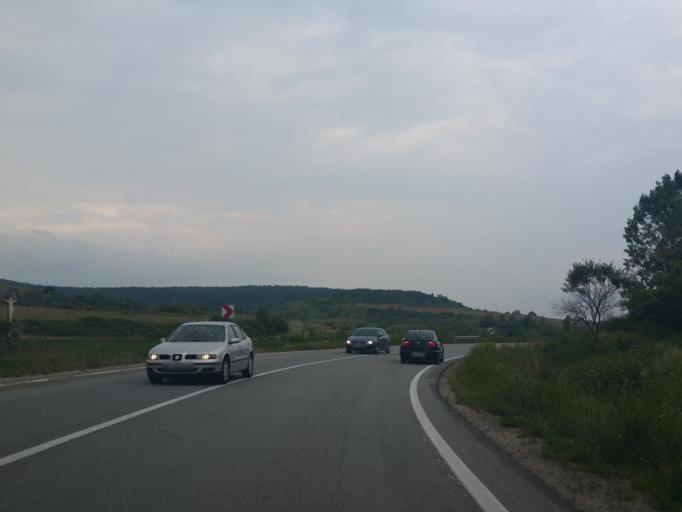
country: RO
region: Salaj
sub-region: Comuna Sanmihaiu Almasului
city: Sanmihaiu Almasului
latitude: 46.9594
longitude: 23.3276
